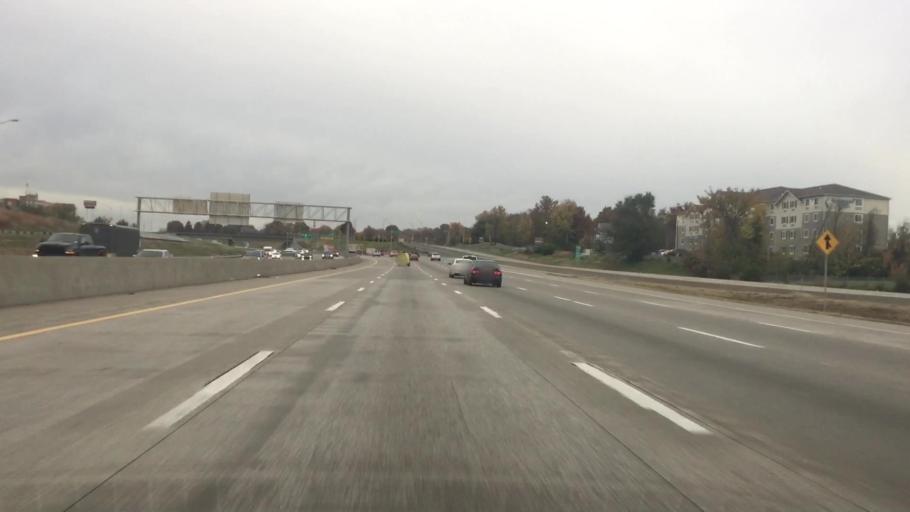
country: US
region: Missouri
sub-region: Jackson County
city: Grandview
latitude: 38.9213
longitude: -94.5279
